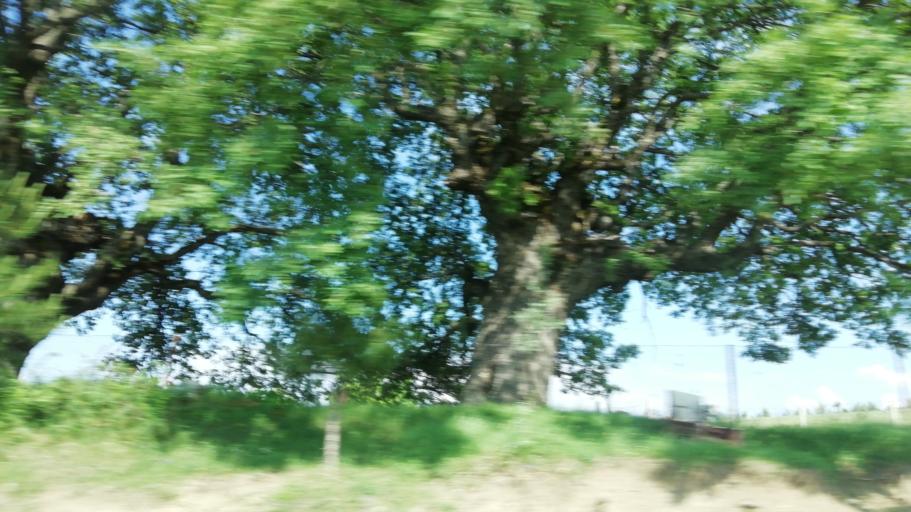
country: TR
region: Karabuk
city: Karabuk
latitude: 41.0903
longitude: 32.5878
